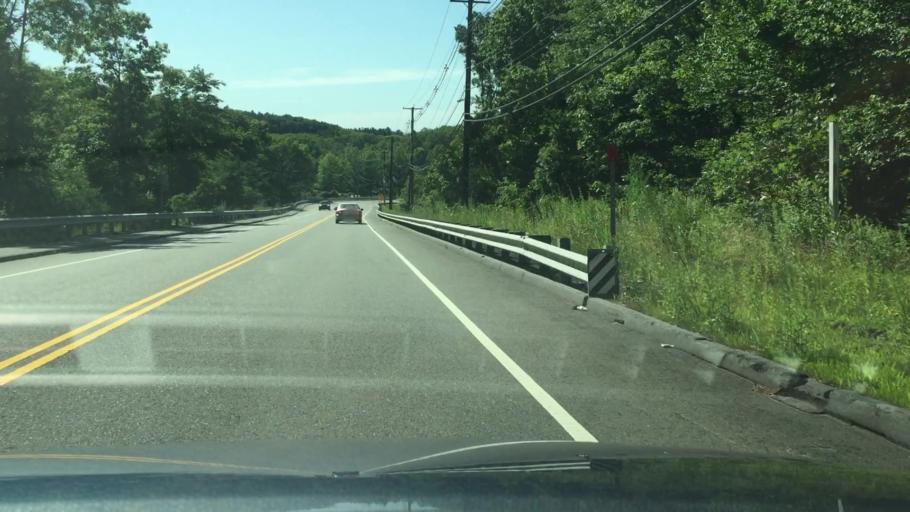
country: US
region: Massachusetts
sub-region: Middlesex County
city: Marlborough
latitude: 42.3259
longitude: -71.5814
